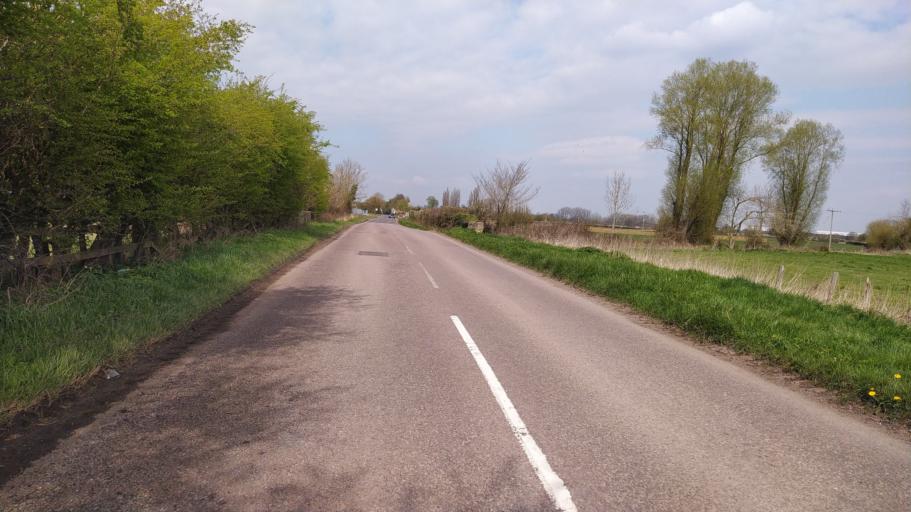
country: GB
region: England
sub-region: Borough of Swindon
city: Wanborough
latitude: 51.5587
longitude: -1.7101
